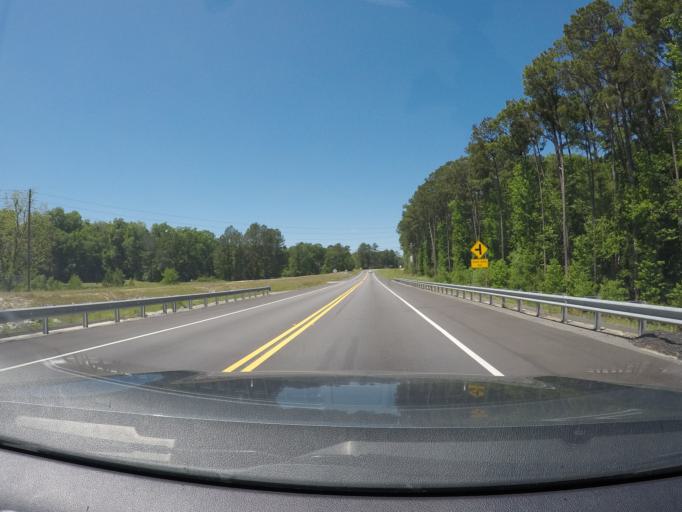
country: US
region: Georgia
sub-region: Chatham County
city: Bloomingdale
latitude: 32.1920
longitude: -81.4177
